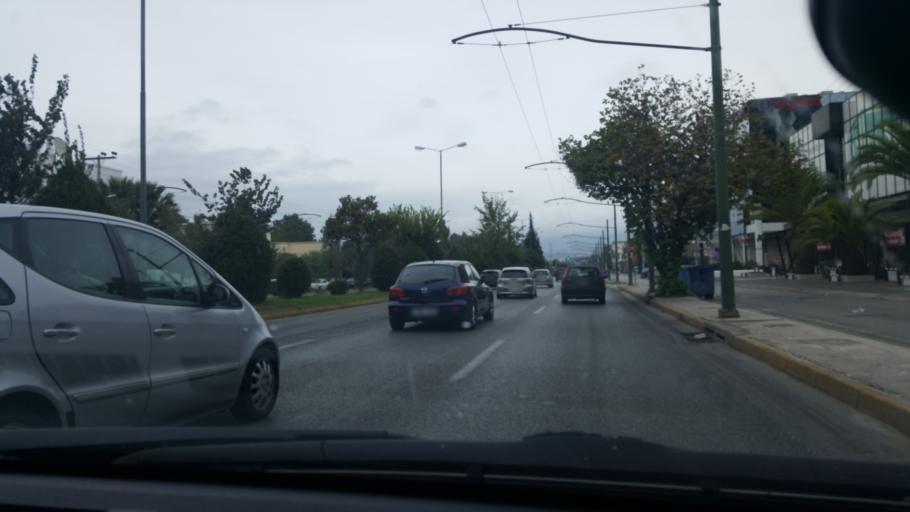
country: GR
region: Attica
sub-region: Nomarchia Athinas
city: Neo Psychiko
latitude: 38.0110
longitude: 23.7812
